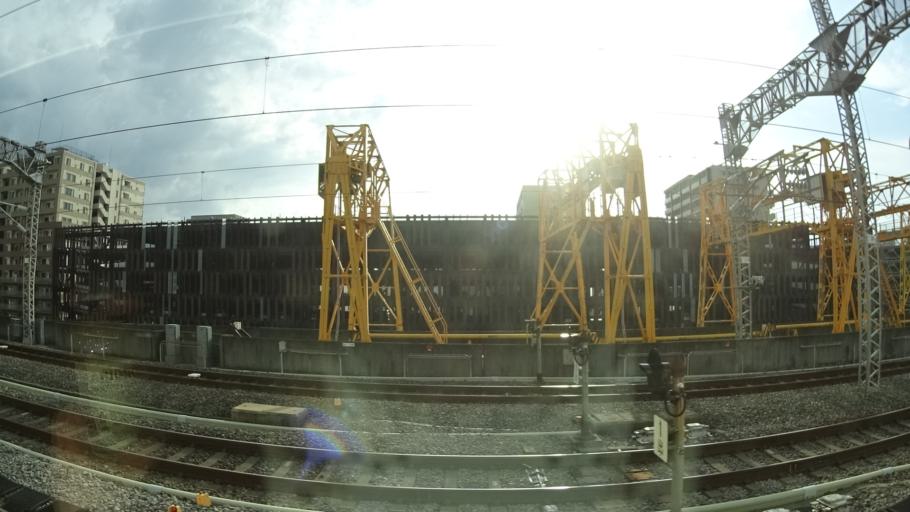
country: JP
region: Gunma
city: Takasaki
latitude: 36.3258
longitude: 139.0126
